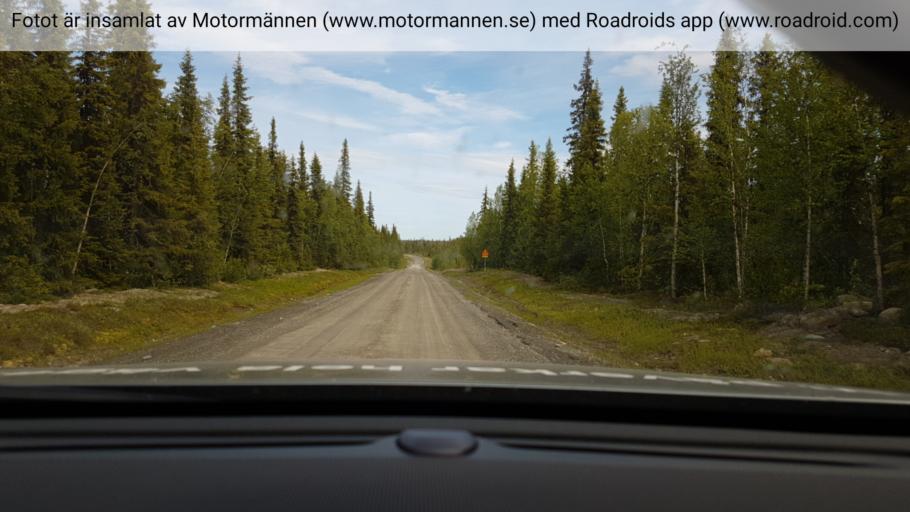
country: SE
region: Vaesterbotten
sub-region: Vilhelmina Kommun
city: Sjoberg
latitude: 65.1633
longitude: 16.3350
